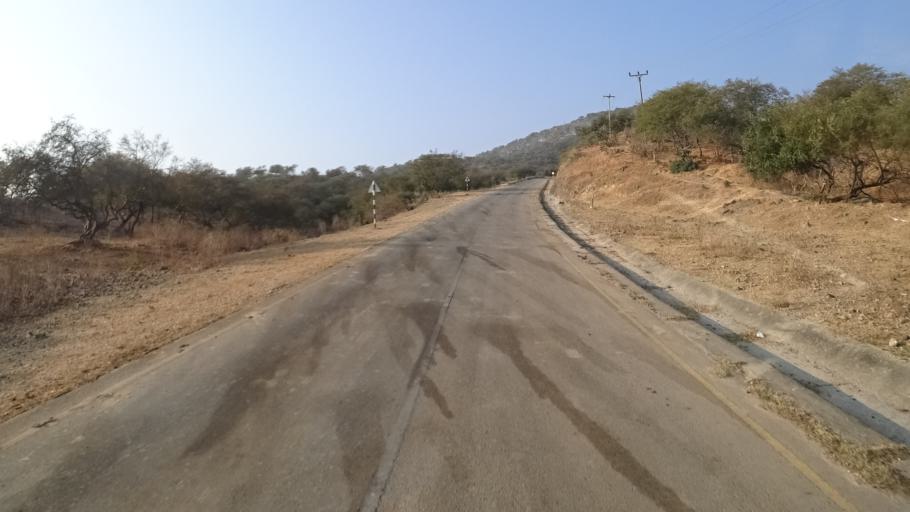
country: YE
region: Al Mahrah
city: Hawf
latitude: 16.7575
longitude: 53.3398
